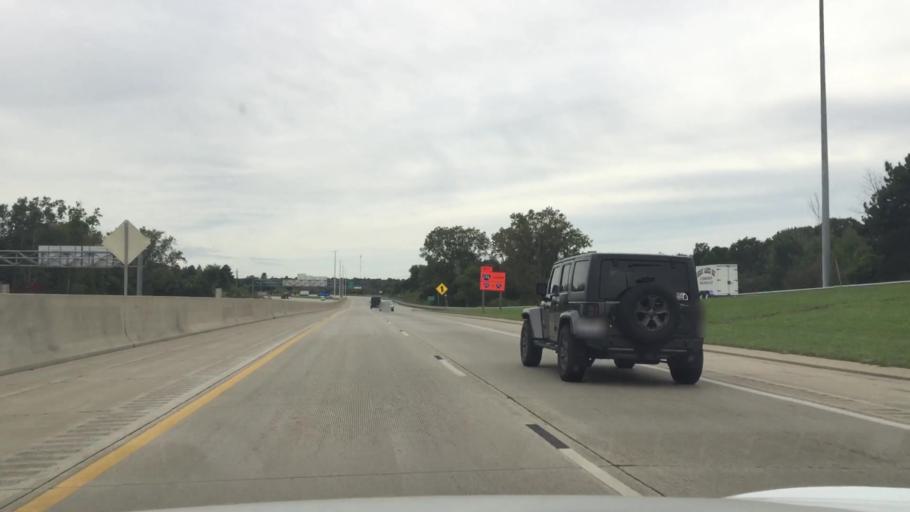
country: US
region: Michigan
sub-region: Saint Clair County
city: Port Huron
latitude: 42.9895
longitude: -82.4598
